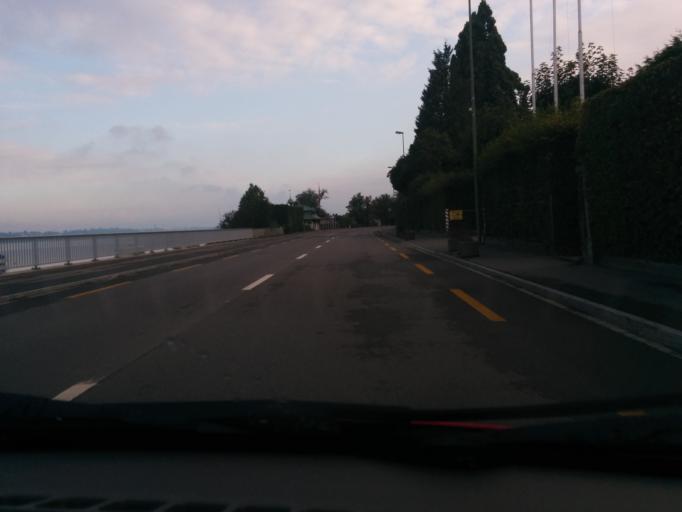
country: CH
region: Zurich
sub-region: Bezirk Meilen
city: Zollikon
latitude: 47.3311
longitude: 8.5723
